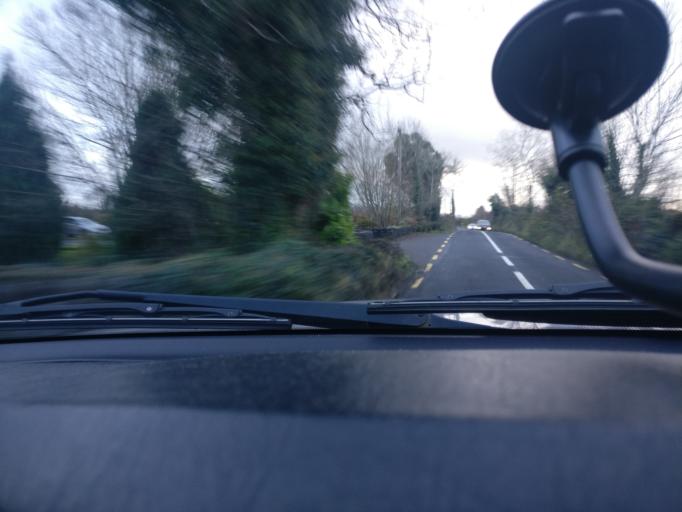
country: IE
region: Connaught
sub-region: County Galway
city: Athenry
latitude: 53.2629
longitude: -8.7416
